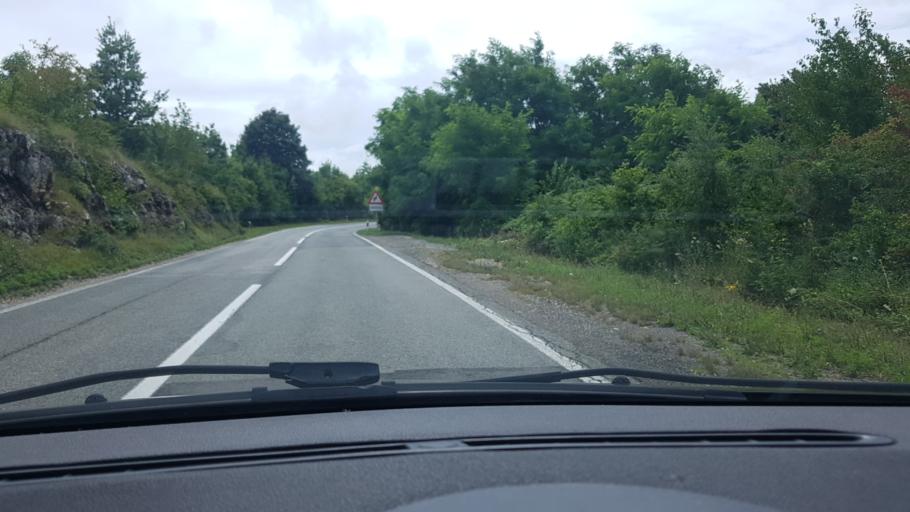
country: HR
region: Licko-Senjska
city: Jezerce
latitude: 44.9443
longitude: 15.6784
